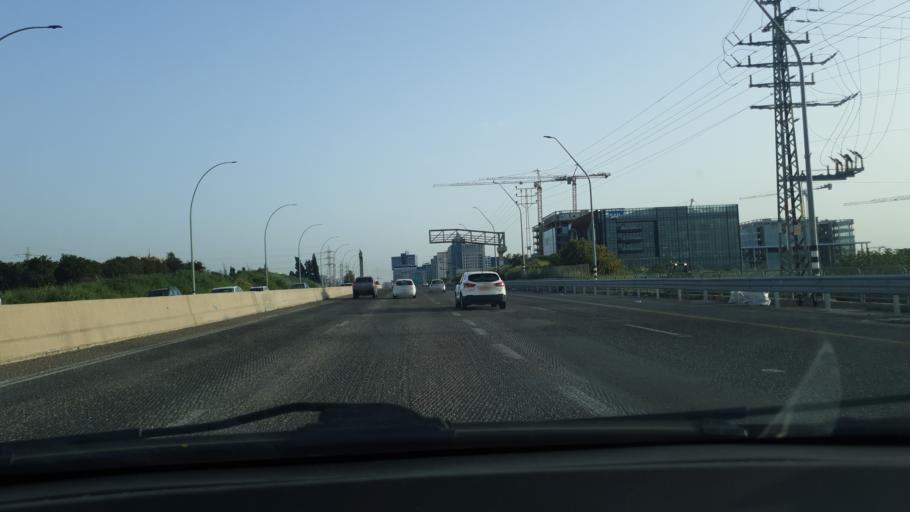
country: IL
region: Central District
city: Ra'anana
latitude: 32.2045
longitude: 34.8842
